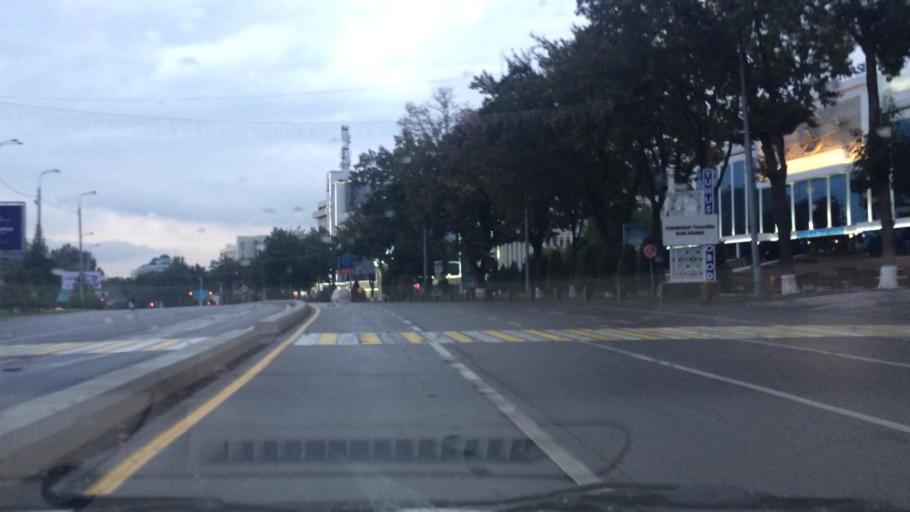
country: UZ
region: Toshkent Shahri
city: Tashkent
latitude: 41.3157
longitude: 69.2843
